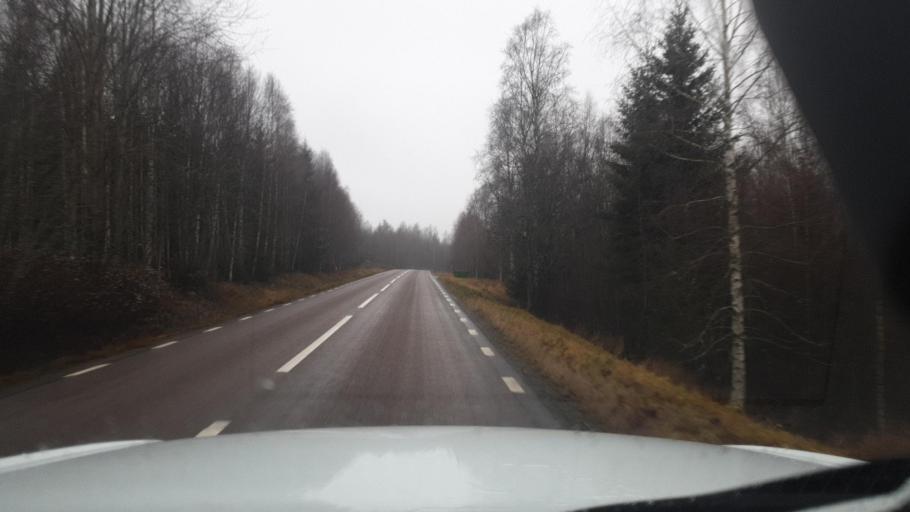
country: SE
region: Vaermland
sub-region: Torsby Kommun
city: Torsby
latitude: 59.9153
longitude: 12.9010
